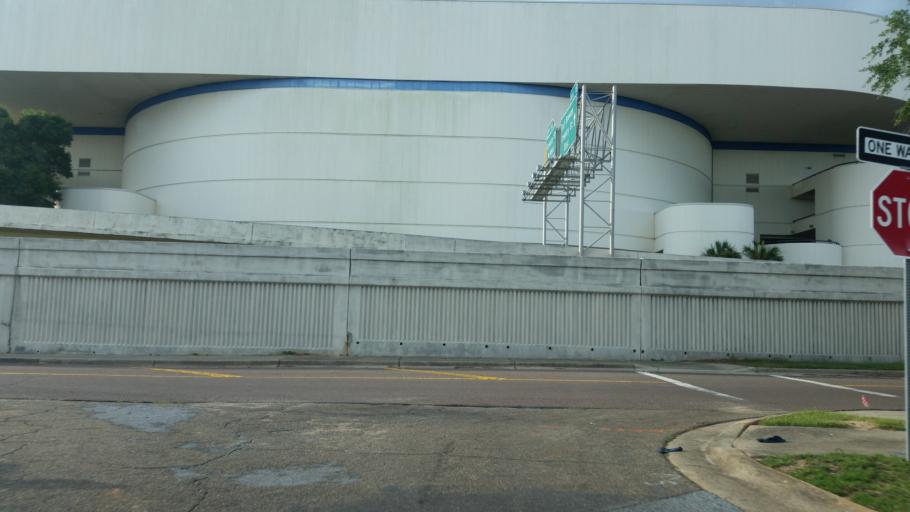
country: US
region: Florida
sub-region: Escambia County
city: Pensacola
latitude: 30.4153
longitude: -87.2087
